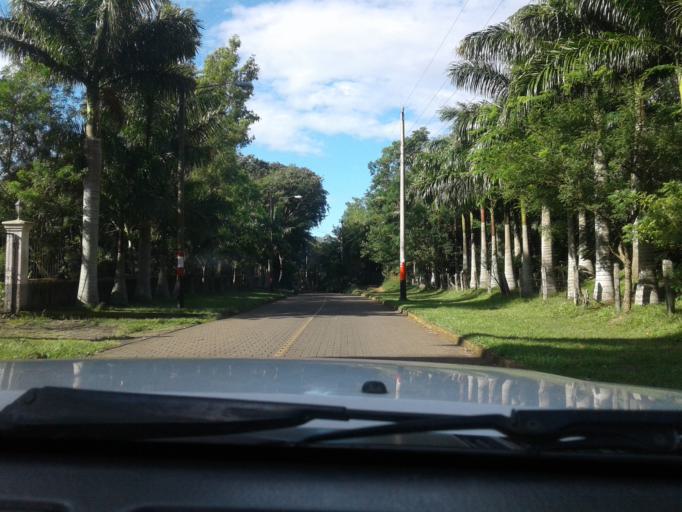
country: NI
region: Carazo
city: Dolores
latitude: 11.8529
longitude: -86.2217
